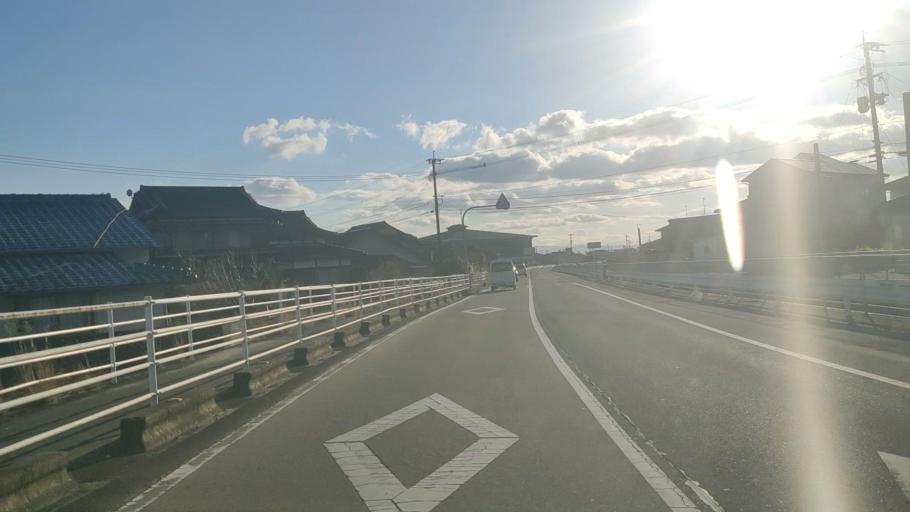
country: JP
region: Saga Prefecture
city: Saga-shi
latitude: 33.2761
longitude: 130.2226
